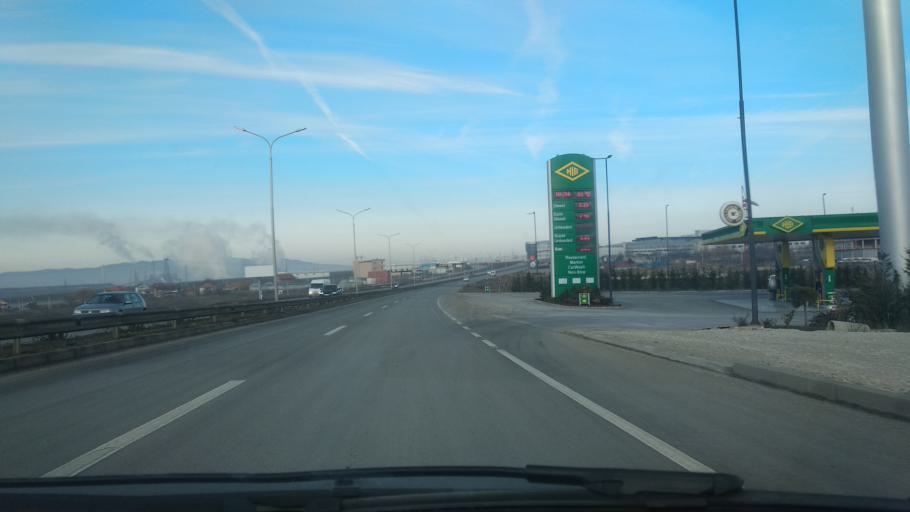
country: XK
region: Pristina
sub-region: Kosovo Polje
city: Kosovo Polje
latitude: 42.6683
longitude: 21.1211
